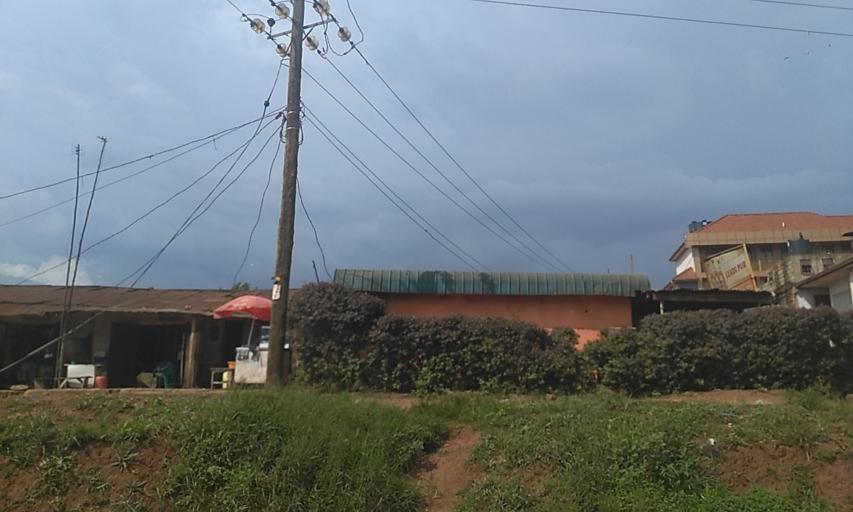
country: UG
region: Central Region
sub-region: Kampala District
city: Kampala
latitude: 0.2945
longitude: 32.5518
